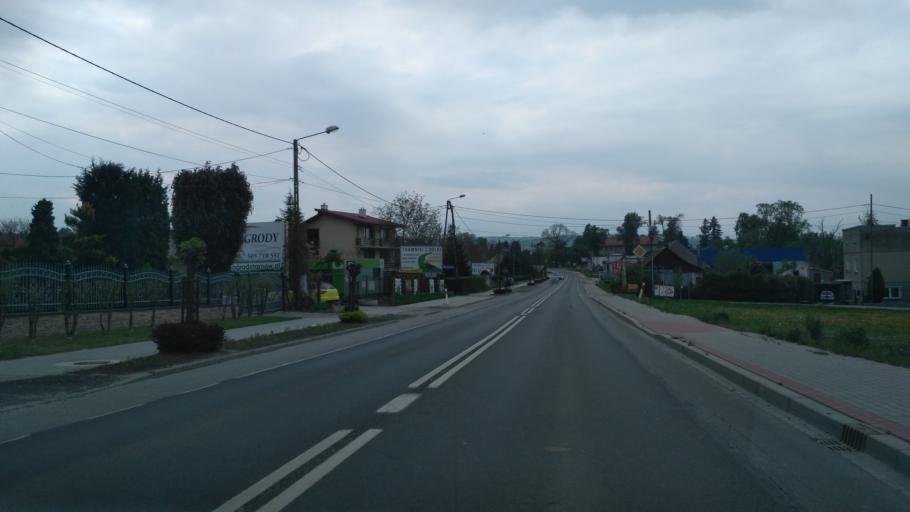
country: PL
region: Lesser Poland Voivodeship
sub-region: Powiat tarnowski
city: Tarnowiec
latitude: 49.9871
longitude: 20.9852
